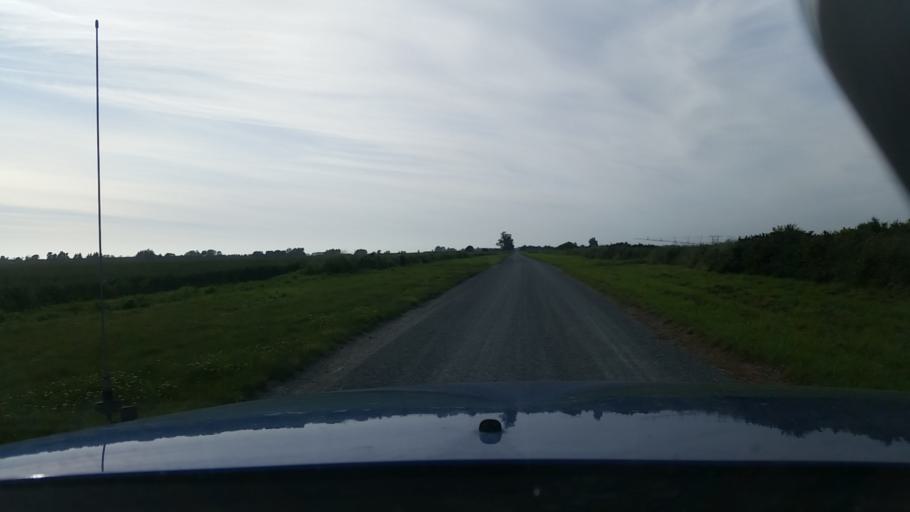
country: NZ
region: Canterbury
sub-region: Ashburton District
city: Tinwald
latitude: -43.9981
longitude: 171.7962
